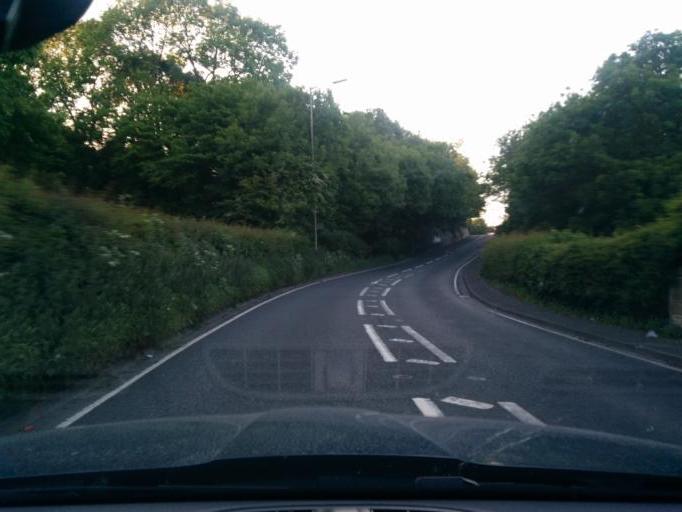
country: GB
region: England
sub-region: Northumberland
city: Bedlington
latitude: 55.1263
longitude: -1.5862
